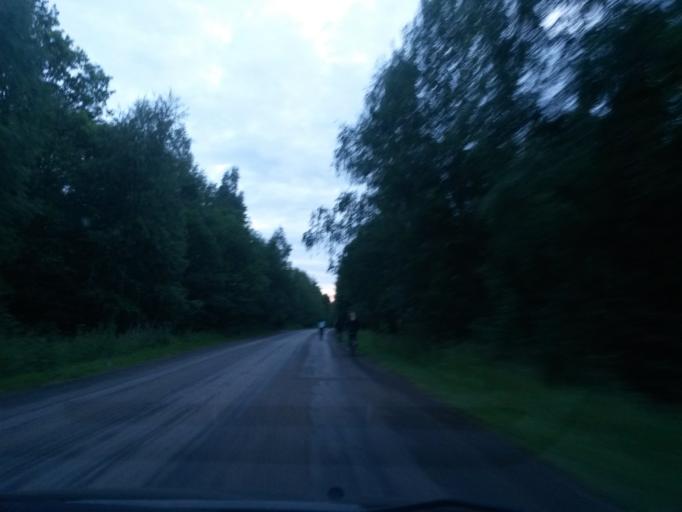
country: RU
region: Moskovskaya
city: Stolbovaya
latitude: 55.2454
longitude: 37.4756
